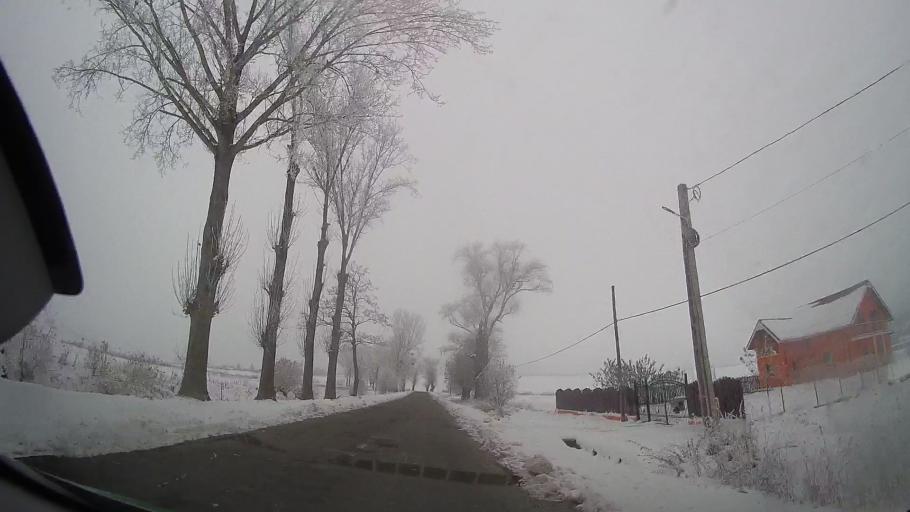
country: RO
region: Neamt
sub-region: Comuna Valea Ursului
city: Chilii
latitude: 46.8523
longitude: 27.0390
